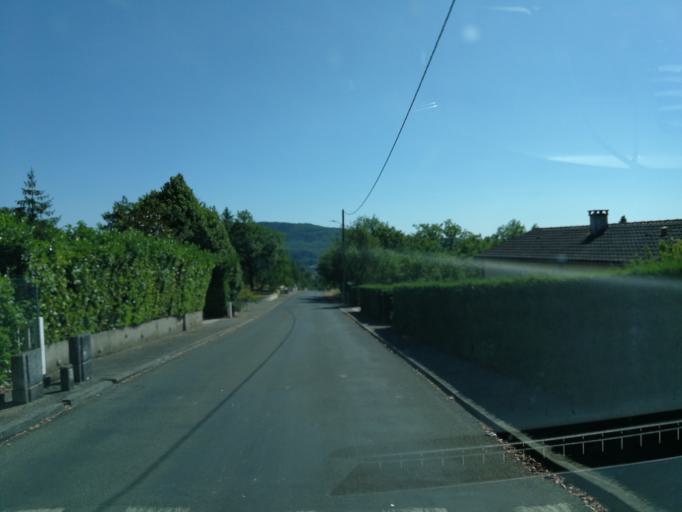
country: FR
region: Midi-Pyrenees
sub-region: Departement du Lot
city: Souillac
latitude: 44.9068
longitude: 1.4809
